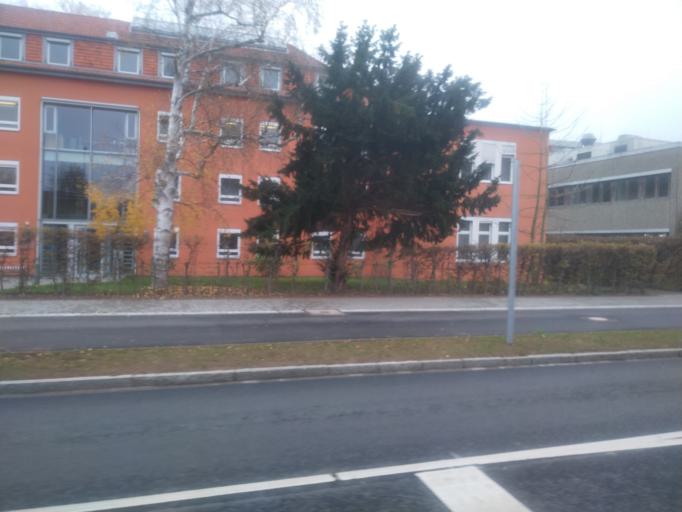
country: DE
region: Lower Saxony
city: Goettingen
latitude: 51.5460
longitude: 9.9398
